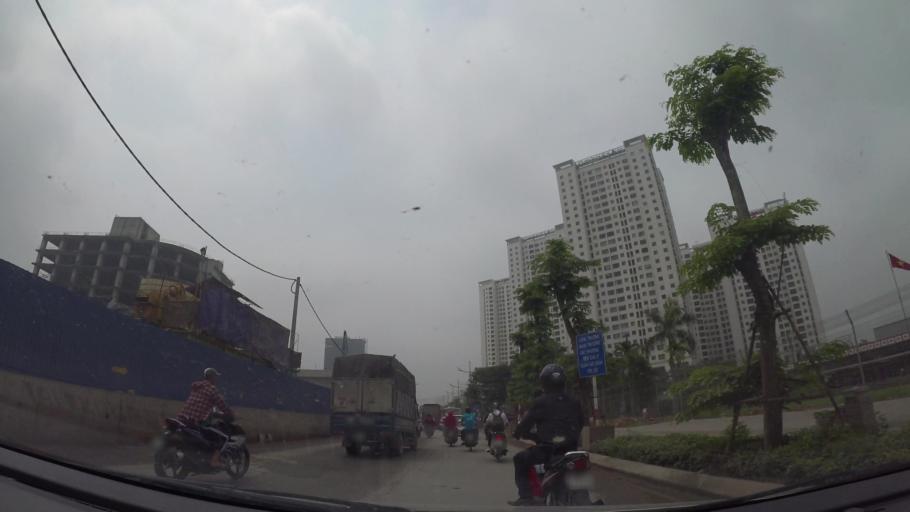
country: VN
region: Ha Noi
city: Cau Dien
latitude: 21.0545
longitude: 105.7817
